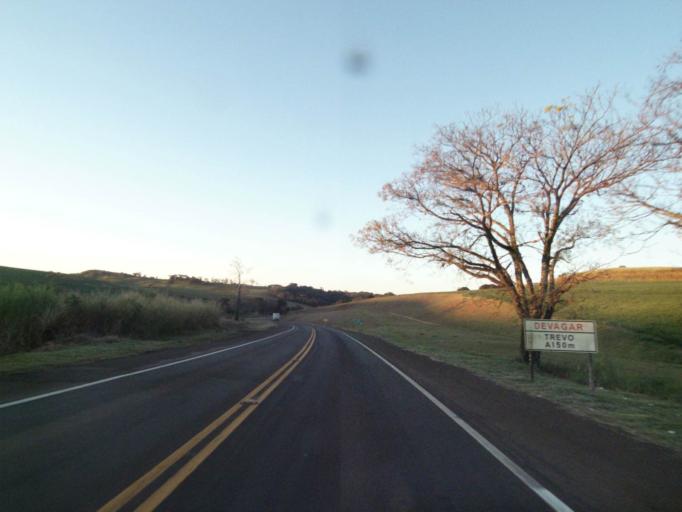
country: BR
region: Parana
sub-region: Londrina
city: Londrina
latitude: -23.5081
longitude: -51.1306
